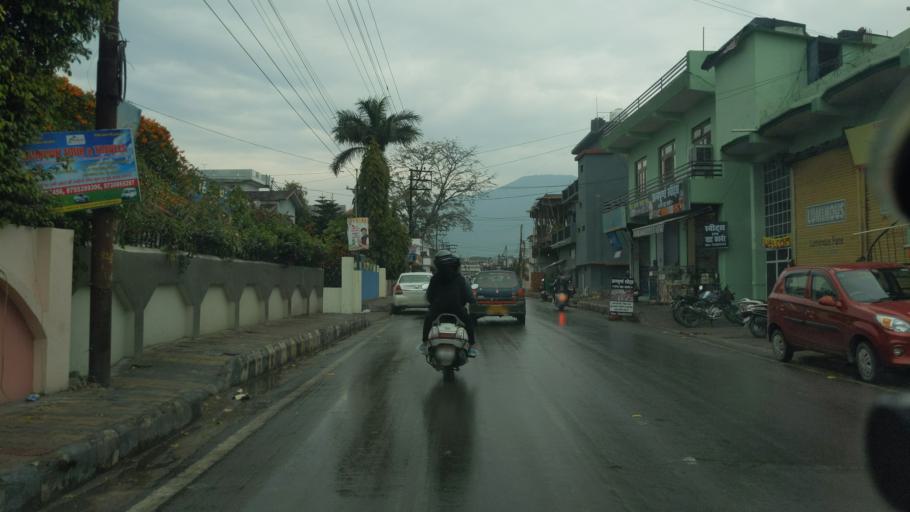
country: IN
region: Uttarakhand
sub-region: Naini Tal
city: Haldwani
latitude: 29.2427
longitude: 79.5300
